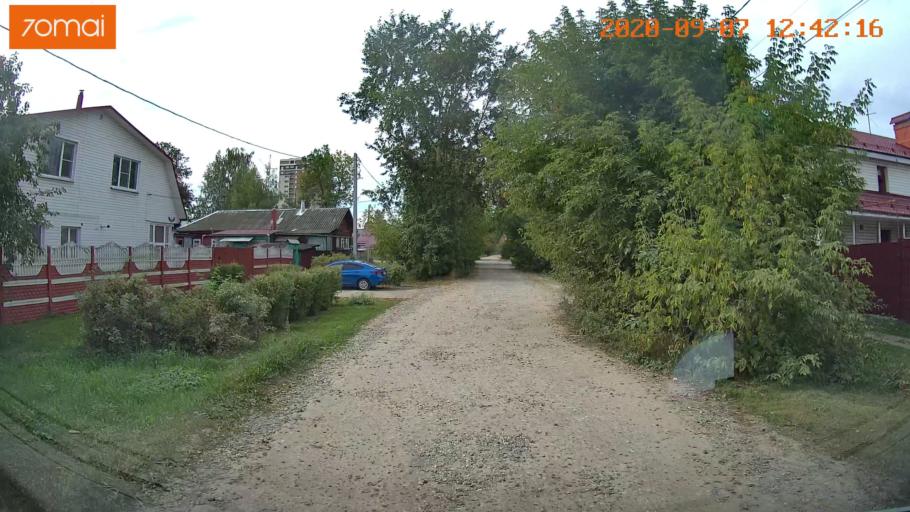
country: RU
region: Ivanovo
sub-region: Gorod Ivanovo
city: Ivanovo
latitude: 56.9737
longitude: 40.9857
